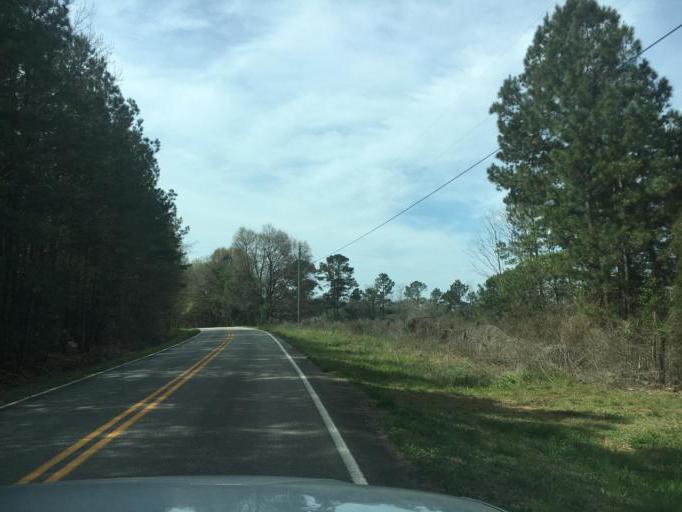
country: US
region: Georgia
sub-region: Franklin County
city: Lavonia
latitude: 34.4194
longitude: -83.0564
